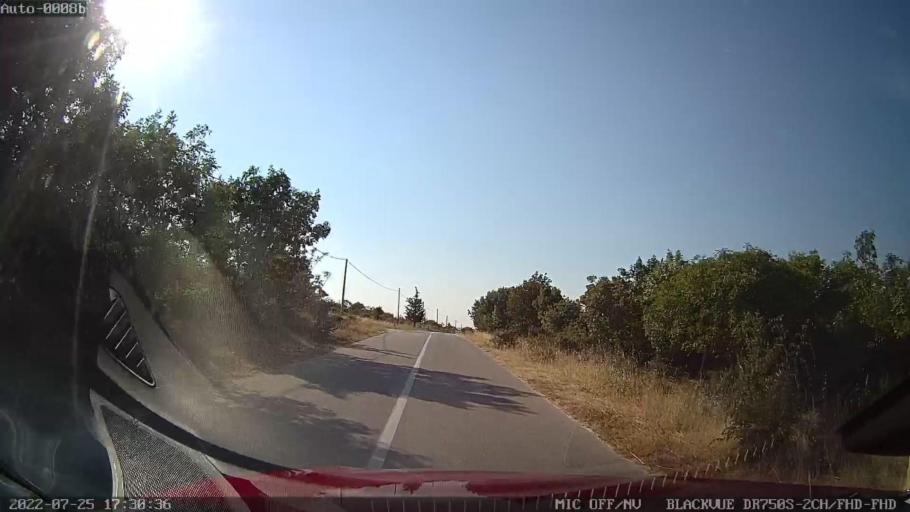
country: HR
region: Zadarska
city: Posedarje
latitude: 44.1650
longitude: 15.5071
